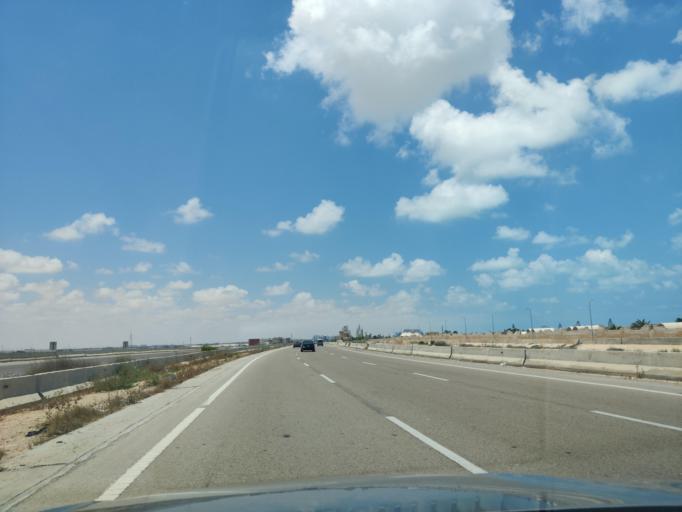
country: EG
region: Muhafazat Matruh
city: Al `Alamayn
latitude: 30.8143
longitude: 29.0421
